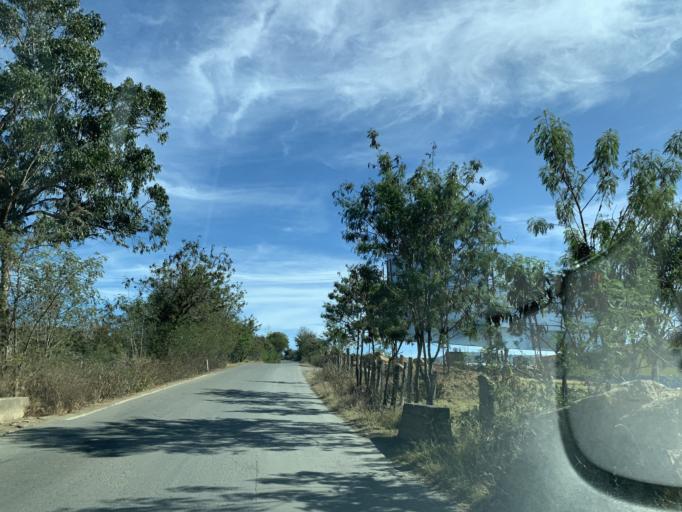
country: CO
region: Boyaca
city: Villa de Leiva
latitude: 5.6633
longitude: -73.5867
